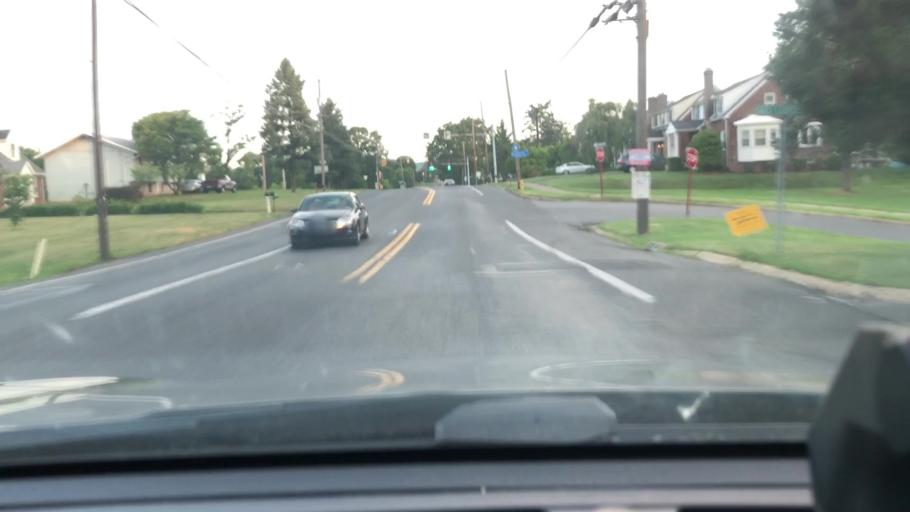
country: US
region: Pennsylvania
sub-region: Northampton County
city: Bethlehem
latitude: 40.6417
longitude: -75.3760
